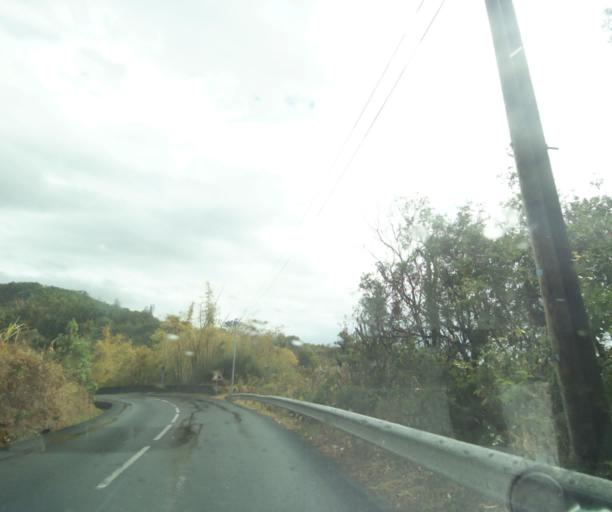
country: RE
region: Reunion
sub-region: Reunion
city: Saint-Paul
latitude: -21.0089
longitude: 55.3163
